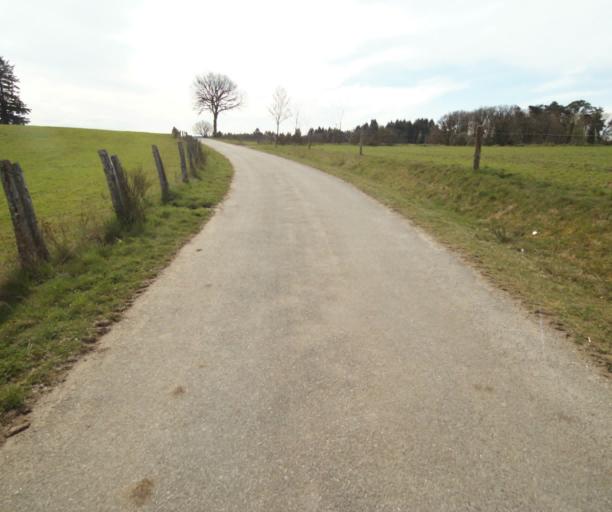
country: FR
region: Limousin
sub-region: Departement de la Correze
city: Correze
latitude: 45.3580
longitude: 1.9095
